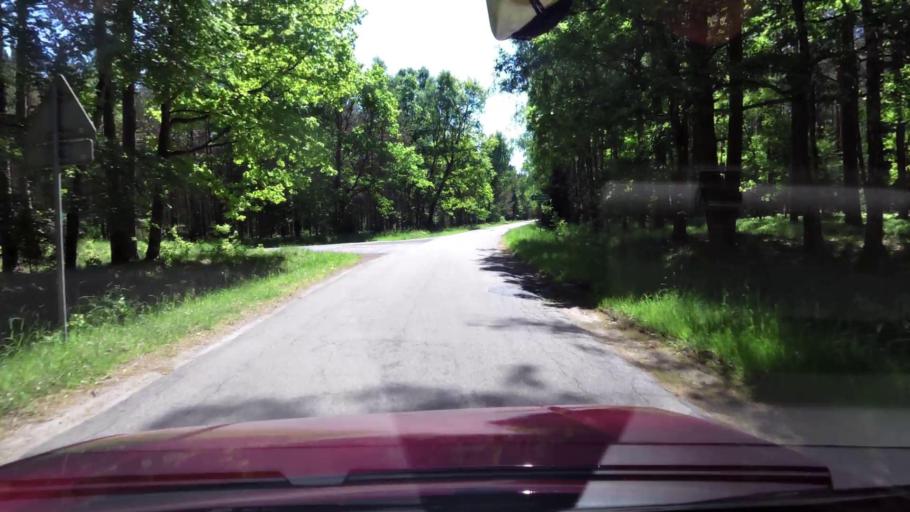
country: PL
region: West Pomeranian Voivodeship
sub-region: Powiat koszalinski
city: Bobolice
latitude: 54.0669
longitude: 16.5653
